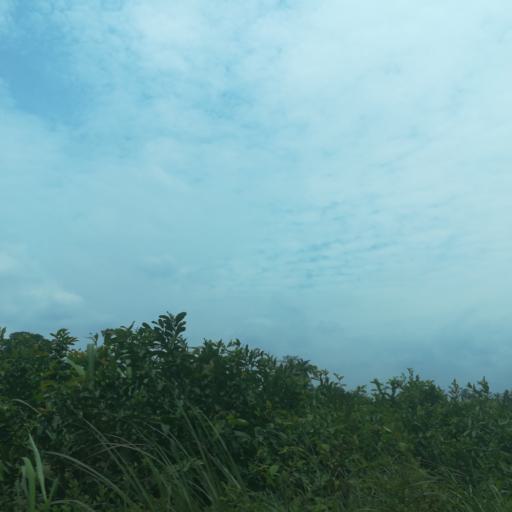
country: NG
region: Lagos
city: Ejirin
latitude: 6.6775
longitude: 3.8001
